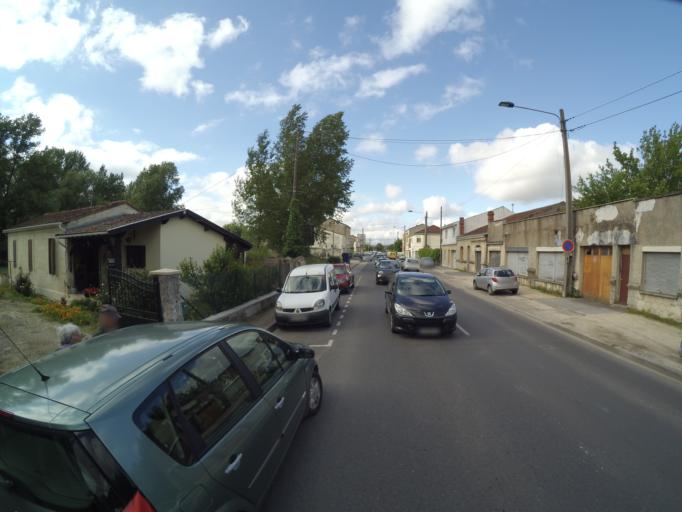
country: FR
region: Aquitaine
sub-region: Departement de la Gironde
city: Lormont
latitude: 44.8779
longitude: -0.5528
